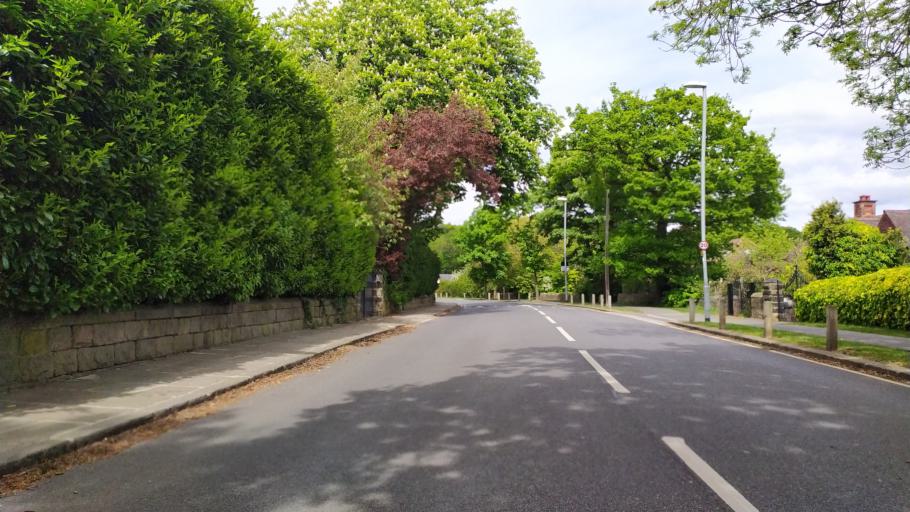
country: GB
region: England
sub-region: City and Borough of Leeds
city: Chapel Allerton
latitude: 53.8322
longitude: -1.5828
